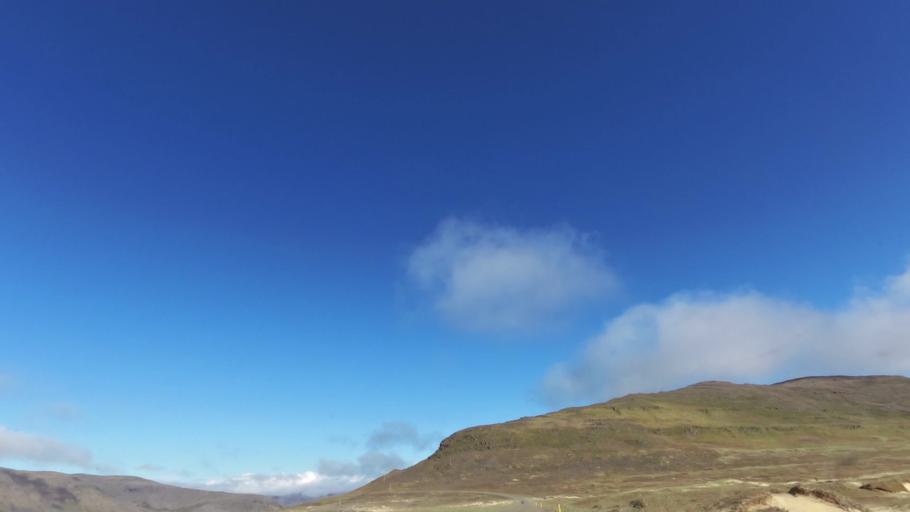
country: IS
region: West
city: Olafsvik
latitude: 65.5554
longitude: -23.9799
